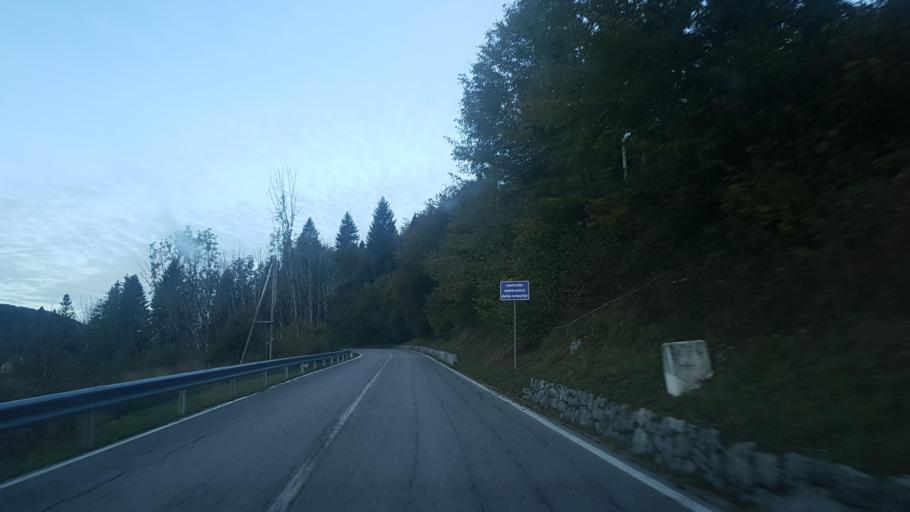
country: IT
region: Friuli Venezia Giulia
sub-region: Provincia di Udine
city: Chiaulis
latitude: 46.3629
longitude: 12.9489
